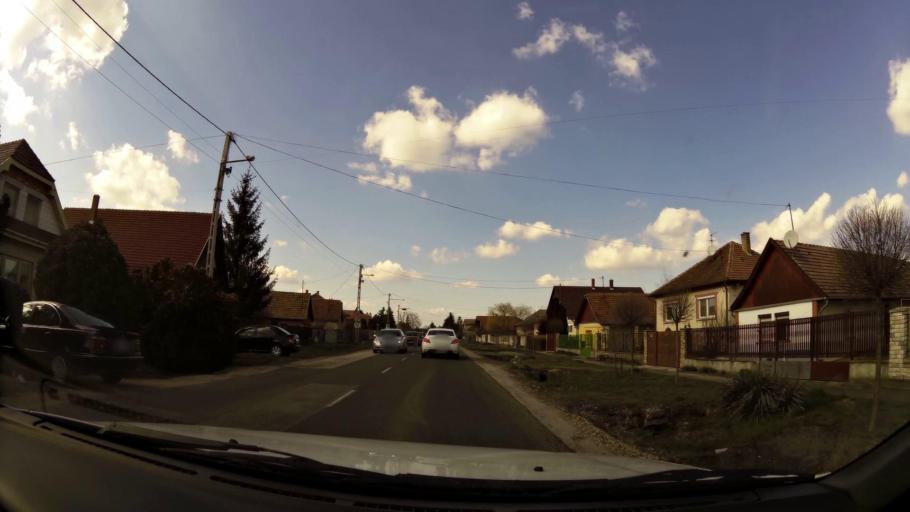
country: HU
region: Pest
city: Szentmartonkata
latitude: 47.4498
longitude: 19.7082
